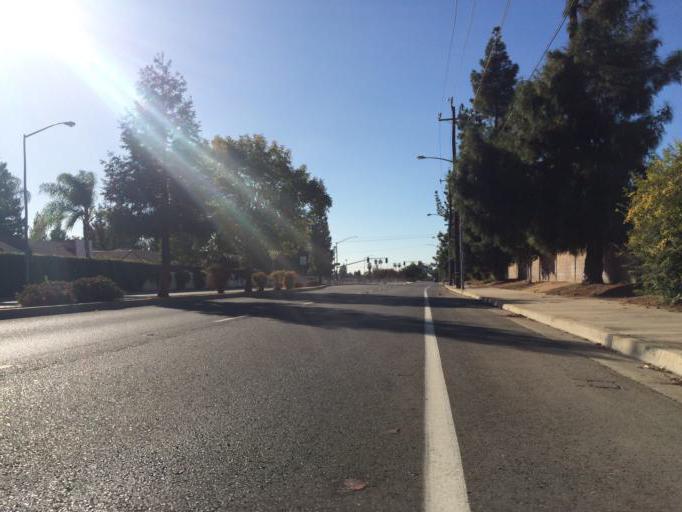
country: US
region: California
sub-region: Fresno County
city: Clovis
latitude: 36.8231
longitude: -119.6801
